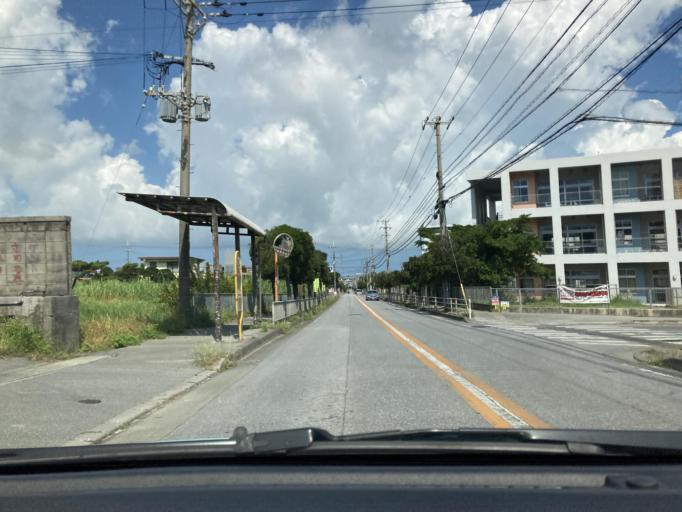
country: JP
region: Okinawa
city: Tomigusuku
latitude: 26.1522
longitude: 127.7517
